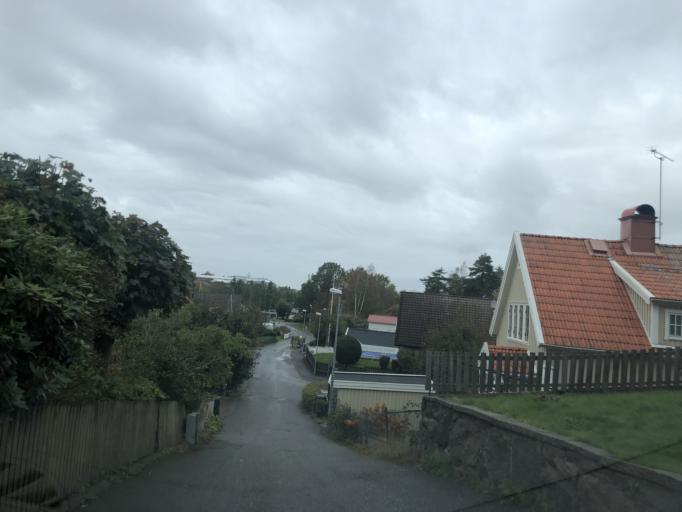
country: SE
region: Vaestra Goetaland
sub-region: Goteborg
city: Majorna
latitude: 57.6705
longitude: 11.8879
